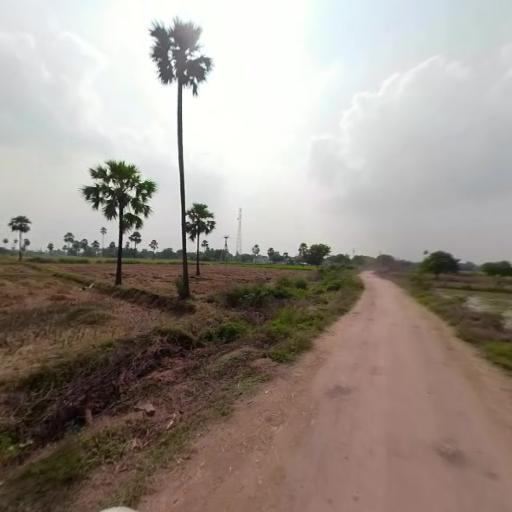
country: IN
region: Telangana
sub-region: Nalgonda
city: Suriapet
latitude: 17.2036
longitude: 79.4836
